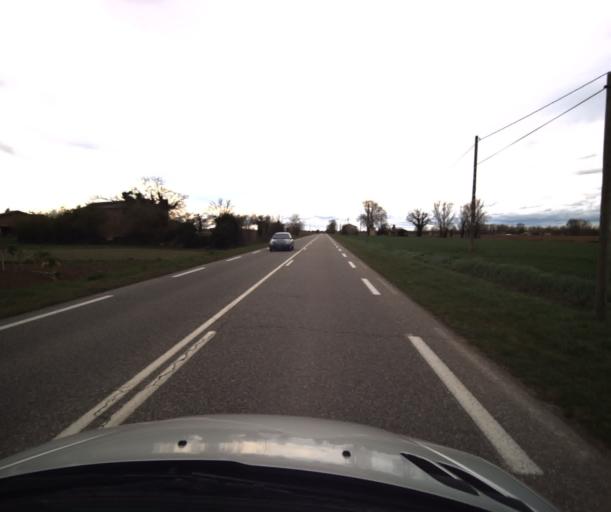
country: FR
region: Midi-Pyrenees
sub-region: Departement du Tarn-et-Garonne
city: Montricoux
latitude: 44.0737
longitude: 1.5788
